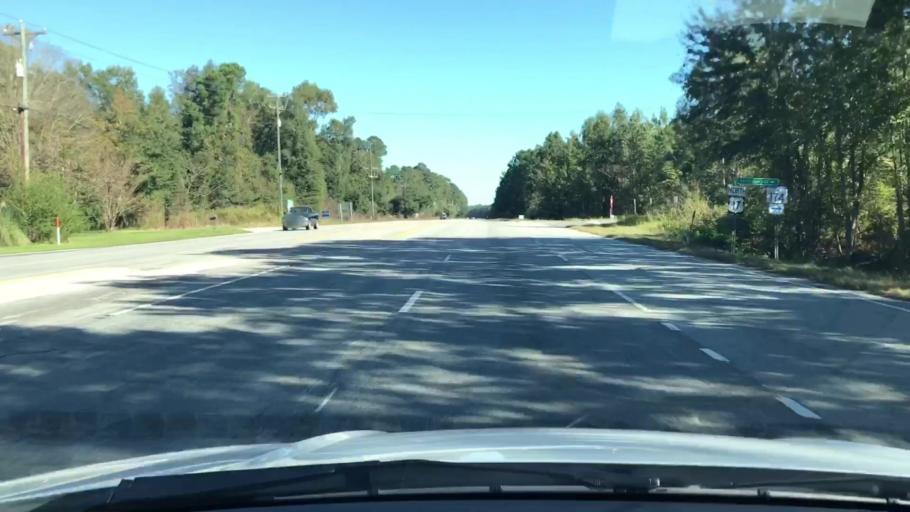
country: US
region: South Carolina
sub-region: Charleston County
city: Ravenel
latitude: 32.7555
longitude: -80.3468
